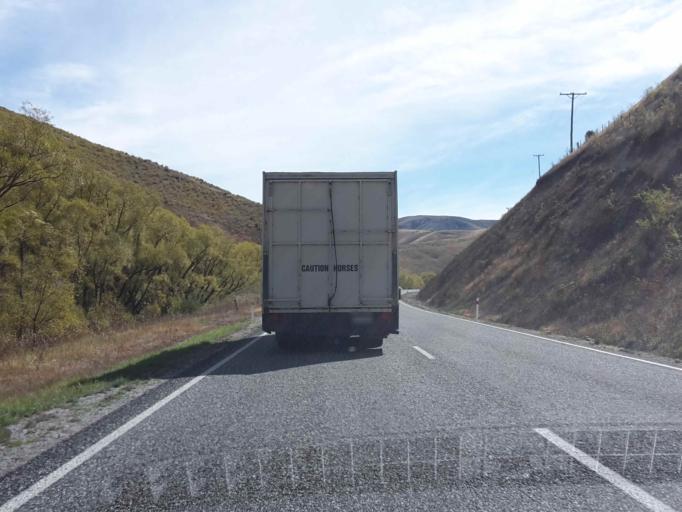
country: NZ
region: Otago
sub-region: Queenstown-Lakes District
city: Wanaka
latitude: -44.6843
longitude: 169.4841
